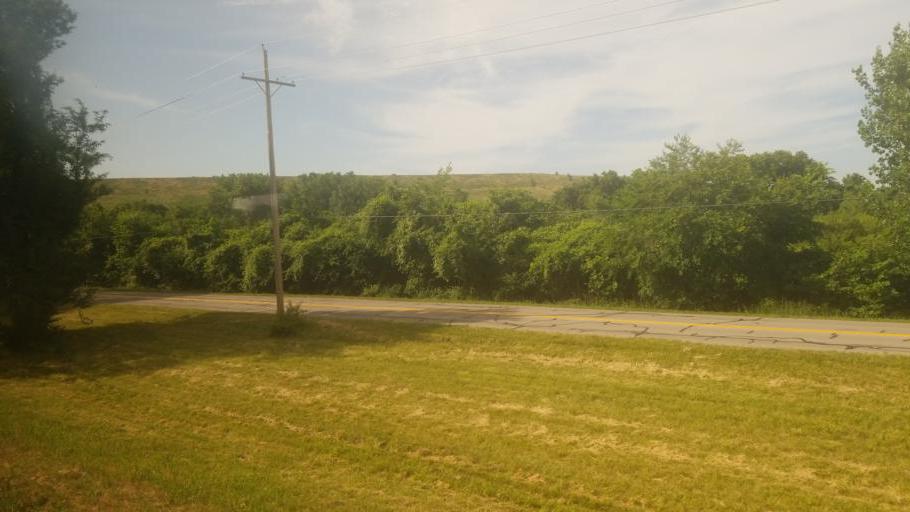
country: US
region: Kansas
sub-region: Wyandotte County
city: Edwardsville
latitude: 39.0418
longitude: -94.8118
